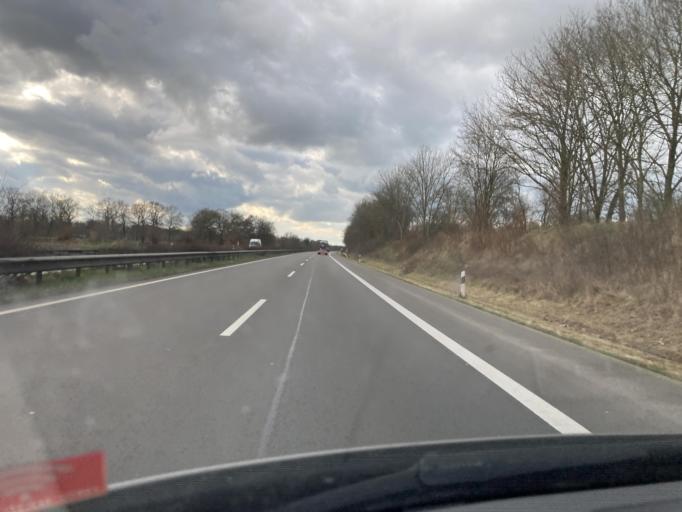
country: DE
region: Lower Saxony
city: Detern
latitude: 53.2485
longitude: 7.7144
